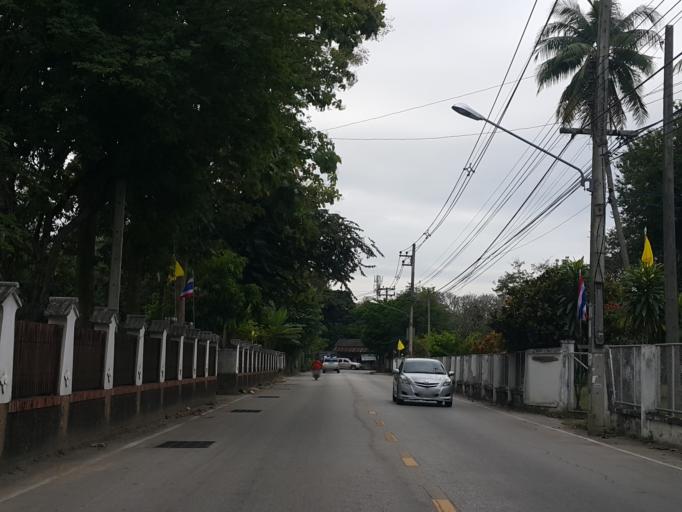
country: TH
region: Lampang
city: Lampang
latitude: 18.2993
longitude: 99.5075
